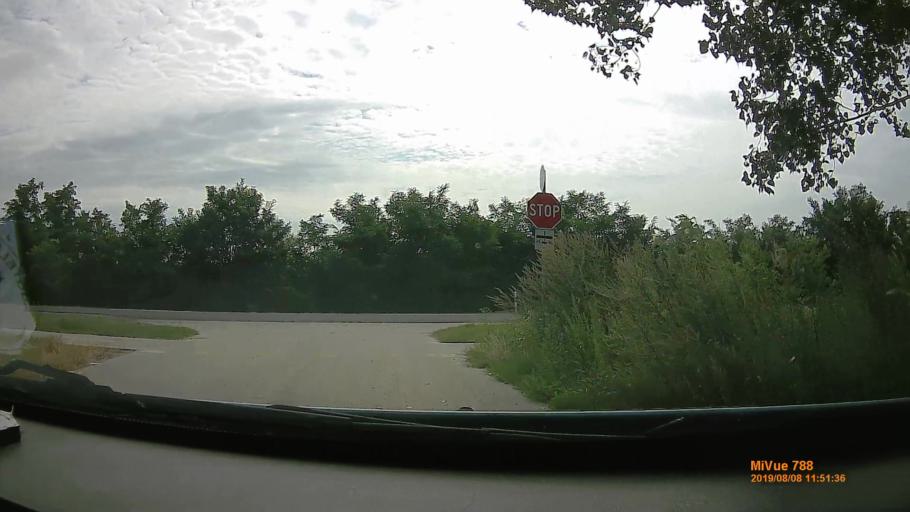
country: HU
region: Szabolcs-Szatmar-Bereg
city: Nyirmihalydi
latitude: 47.7247
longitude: 21.9483
